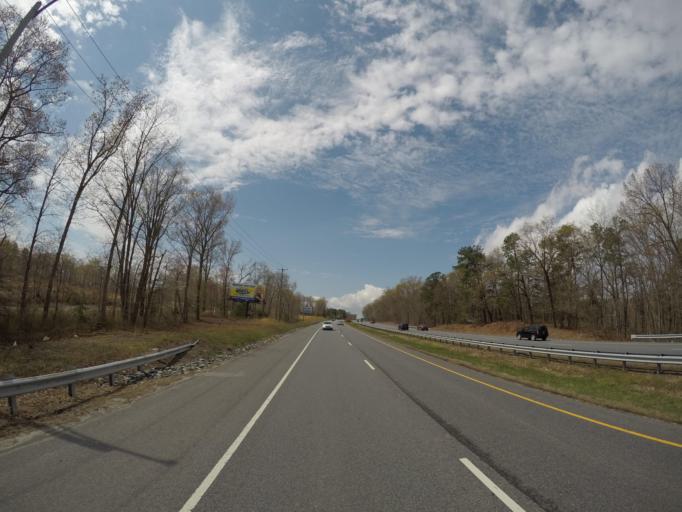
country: US
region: Maryland
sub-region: Cecil County
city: Charlestown
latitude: 39.5856
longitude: -76.0089
